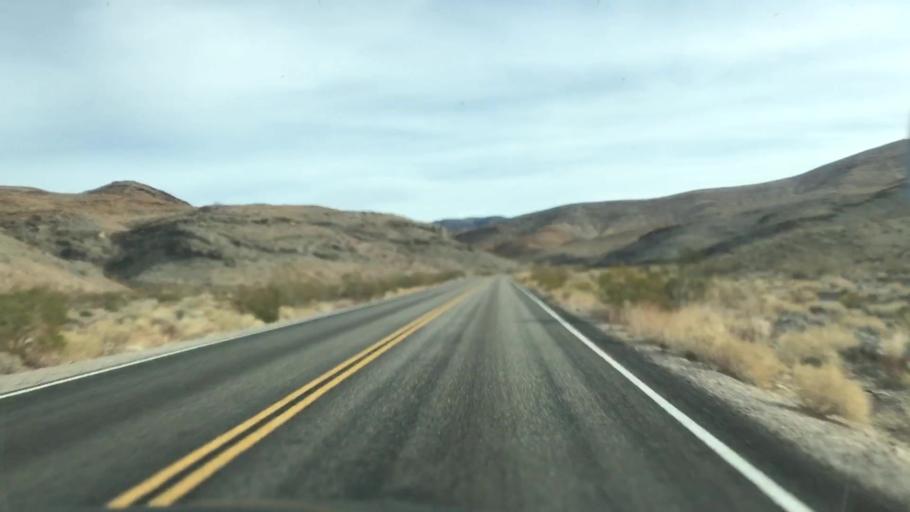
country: US
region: Nevada
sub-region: Nye County
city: Beatty
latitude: 36.7425
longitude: -116.9631
